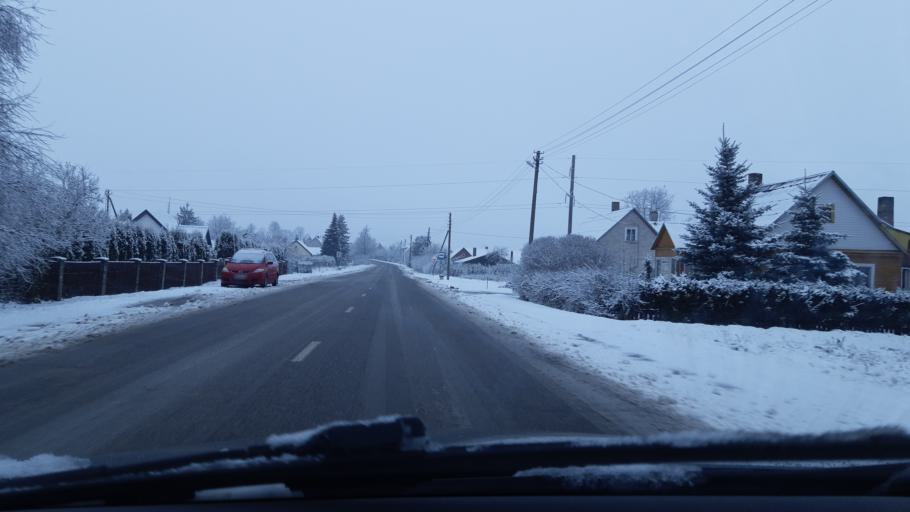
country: LT
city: Kaisiadorys
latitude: 54.8435
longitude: 24.3427
